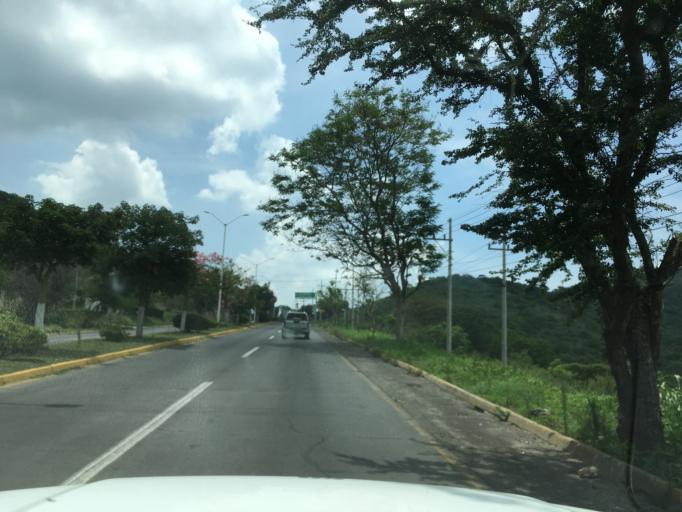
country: MX
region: Jalisco
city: Tlajomulco de Zuniga
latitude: 20.4902
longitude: -103.4703
